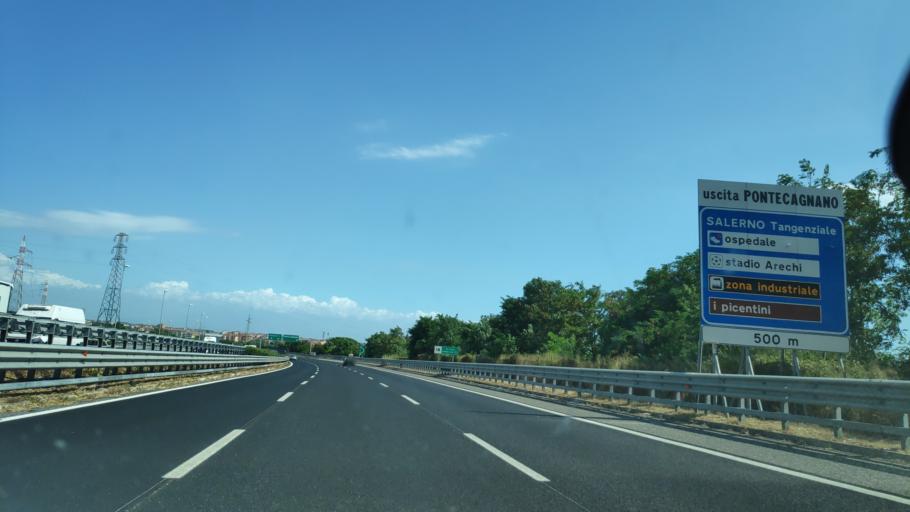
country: IT
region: Campania
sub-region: Provincia di Salerno
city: Pontecagnano
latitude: 40.6591
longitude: 14.8615
